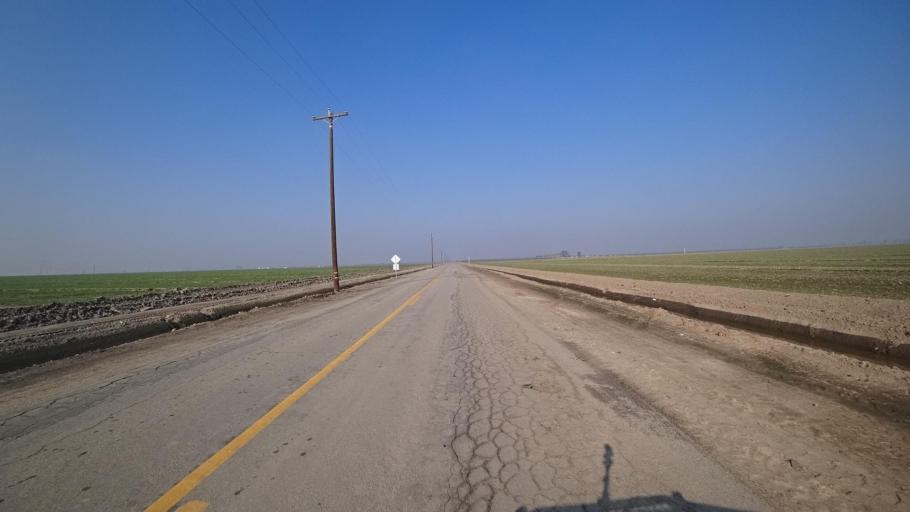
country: US
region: California
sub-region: Kern County
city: Greenfield
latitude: 35.1803
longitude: -119.0437
